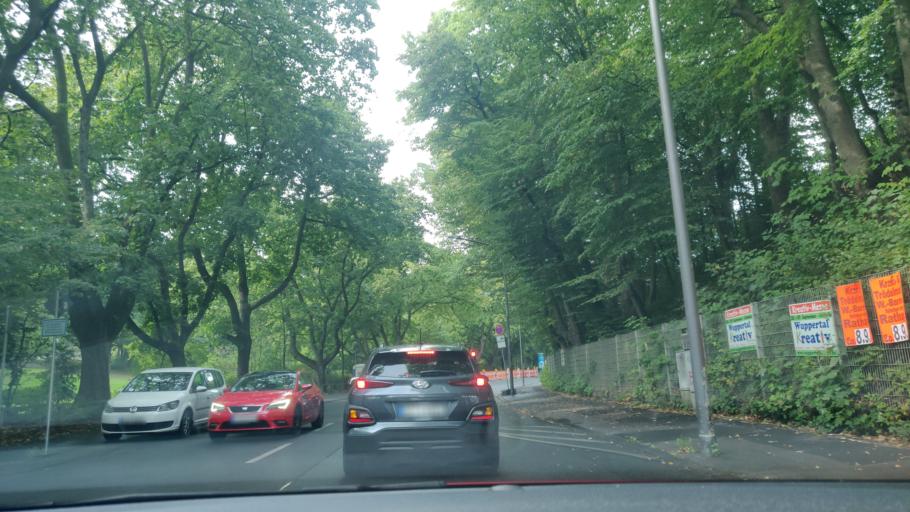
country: DE
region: North Rhine-Westphalia
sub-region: Regierungsbezirk Dusseldorf
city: Wuppertal
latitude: 51.2739
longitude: 7.1230
